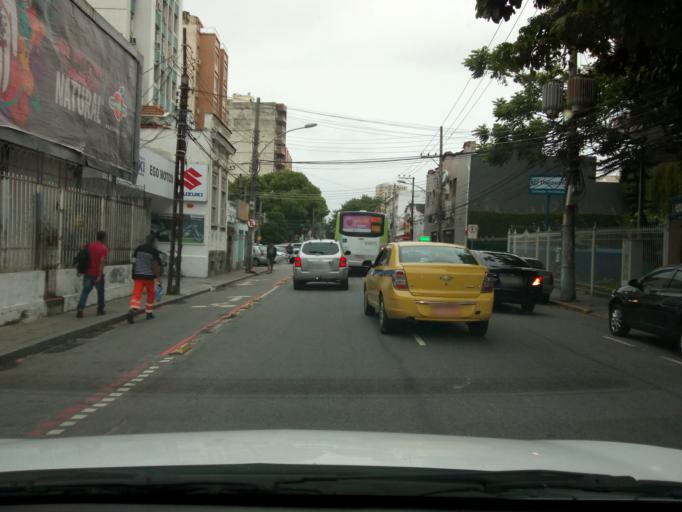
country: BR
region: Rio de Janeiro
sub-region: Rio De Janeiro
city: Rio de Janeiro
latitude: -22.9206
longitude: -43.2315
